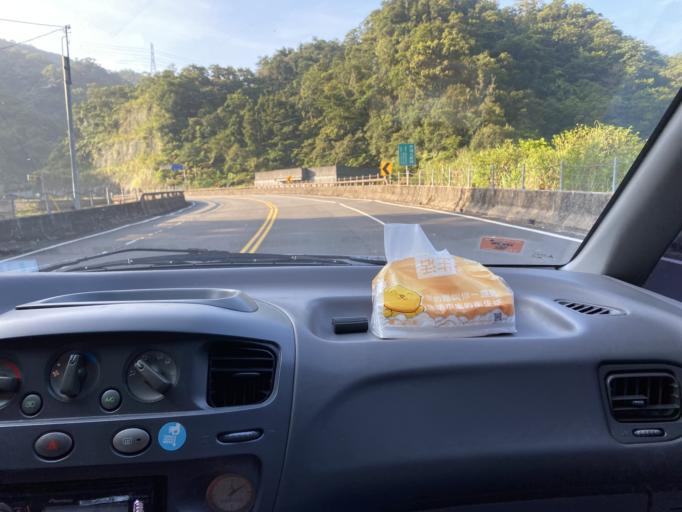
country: TW
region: Taiwan
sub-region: Keelung
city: Keelung
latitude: 25.0264
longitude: 121.7805
